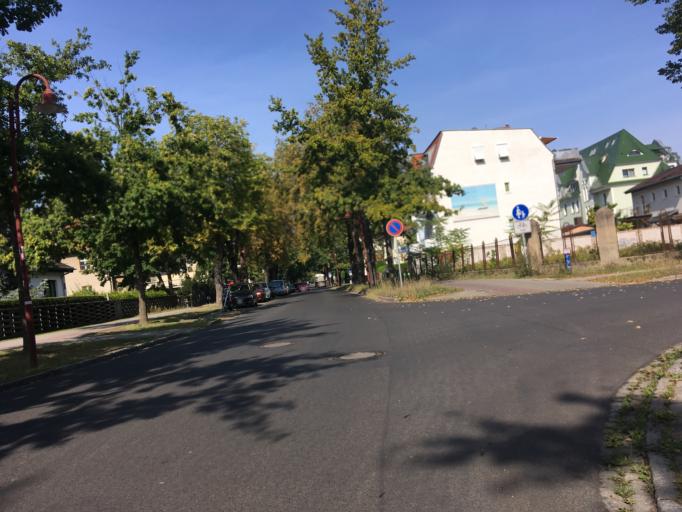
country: DE
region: Brandenburg
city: Zeuthen
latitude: 52.3731
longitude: 13.6209
